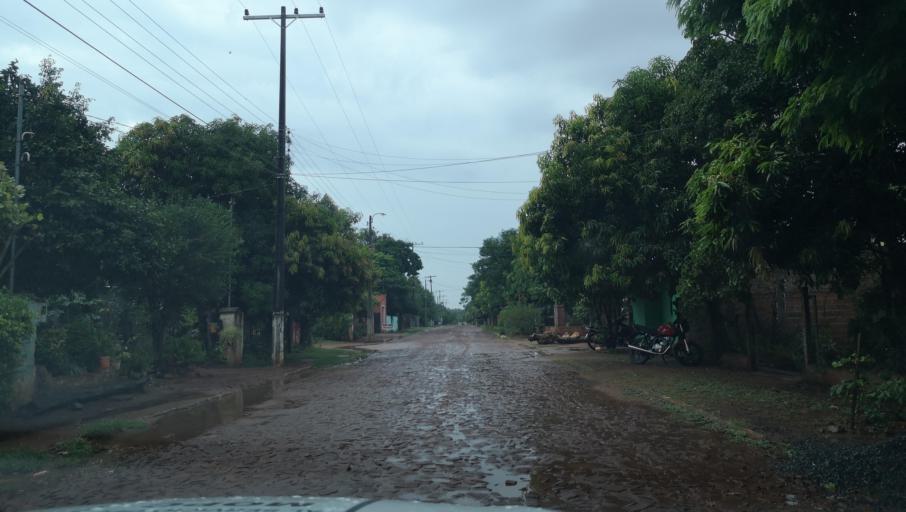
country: PY
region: Misiones
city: Santa Maria
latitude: -26.9013
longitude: -57.0384
